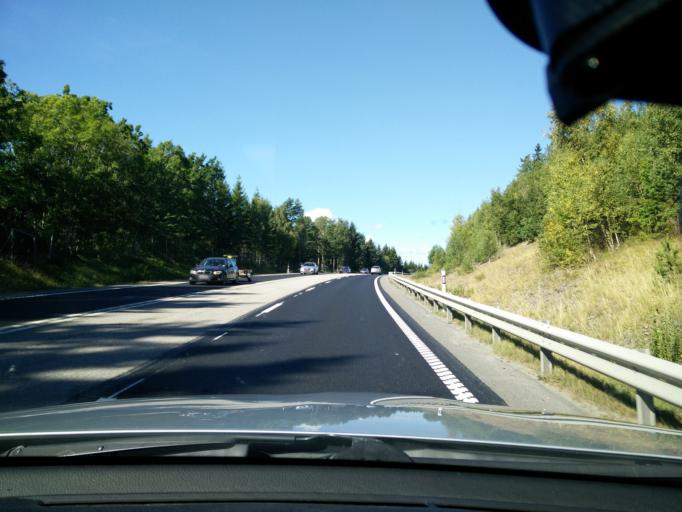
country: SE
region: Stockholm
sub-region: Lidingo
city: Lidingoe
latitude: 59.4528
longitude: 18.1854
